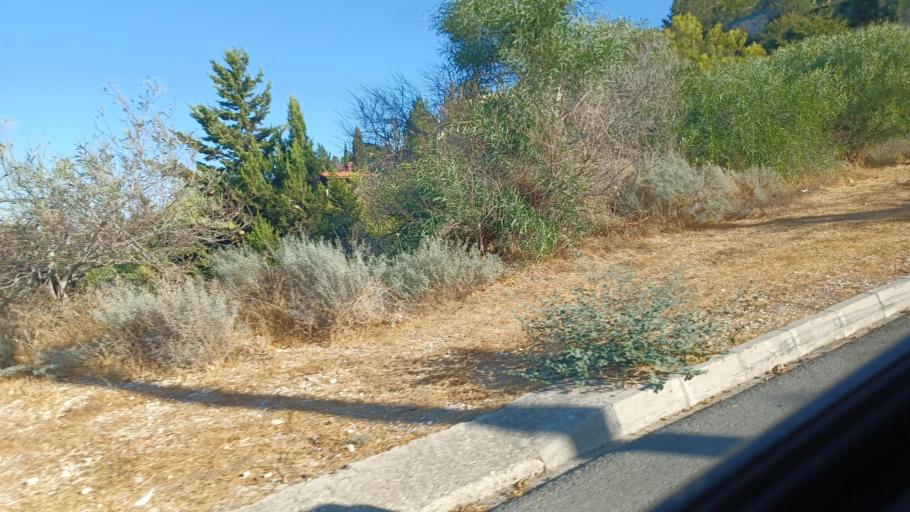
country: CY
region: Pafos
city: Tala
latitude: 34.8466
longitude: 32.4409
